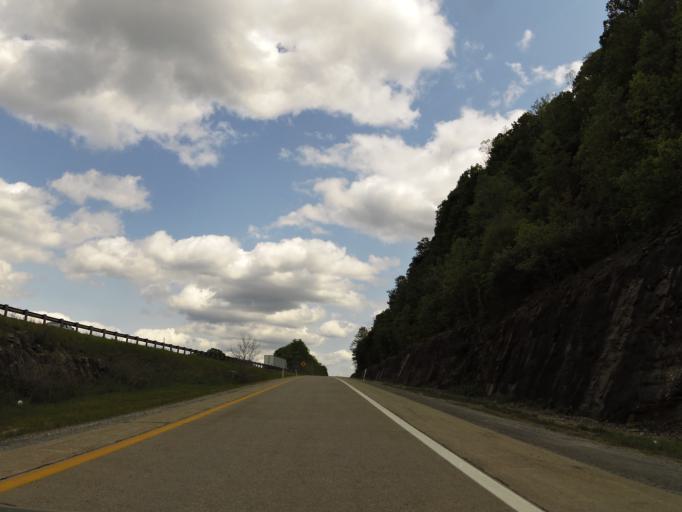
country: US
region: West Virginia
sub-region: Fayette County
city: Oak Hill
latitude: 37.9721
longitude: -81.2828
